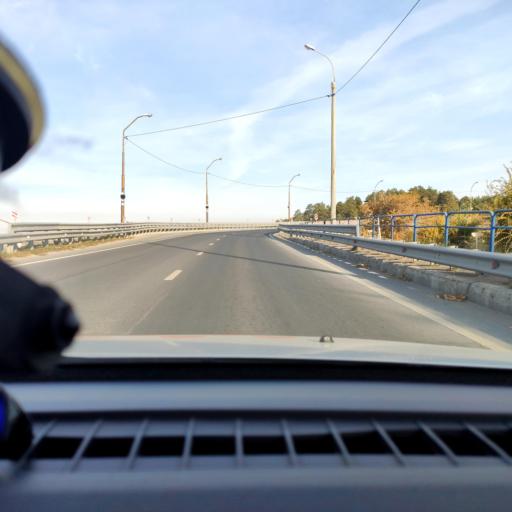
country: RU
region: Samara
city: Volzhskiy
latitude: 53.4324
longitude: 50.1172
